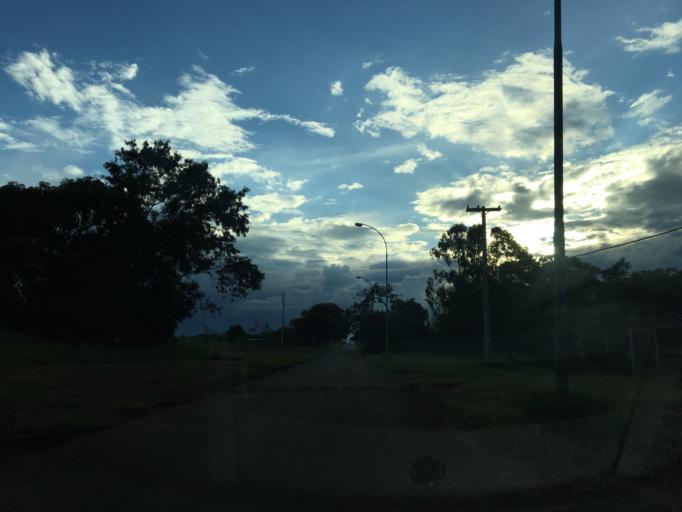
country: BR
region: Federal District
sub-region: Brasilia
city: Brasilia
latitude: -15.8033
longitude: -47.8342
